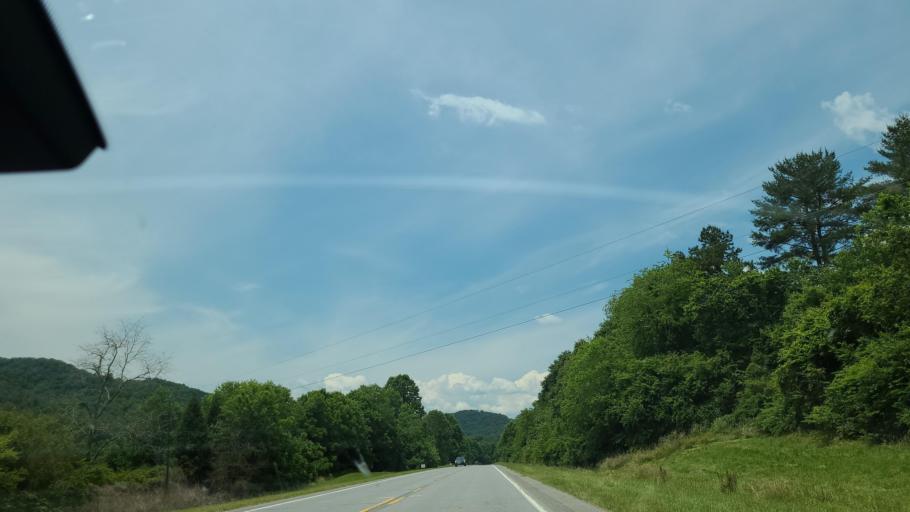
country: US
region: Georgia
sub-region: Towns County
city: Hiawassee
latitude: 35.0242
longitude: -83.6838
